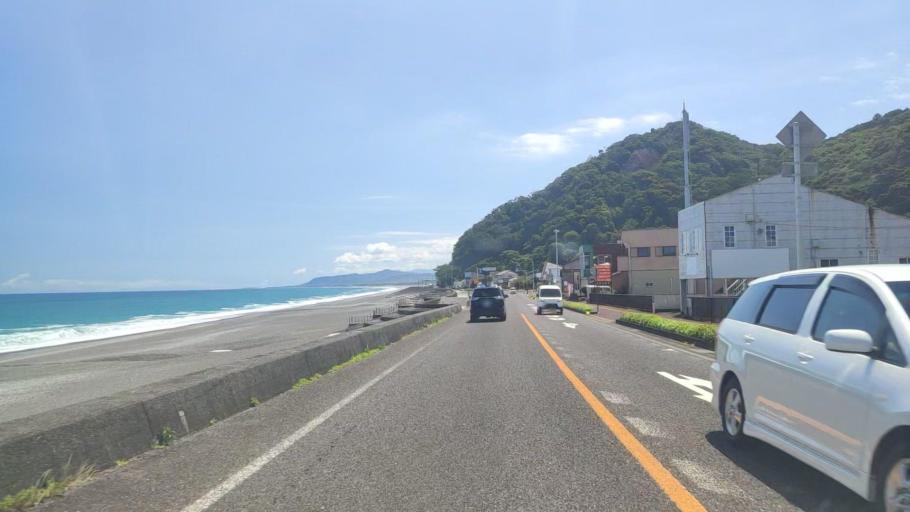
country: JP
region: Wakayama
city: Shingu
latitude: 33.8827
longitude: 136.0967
